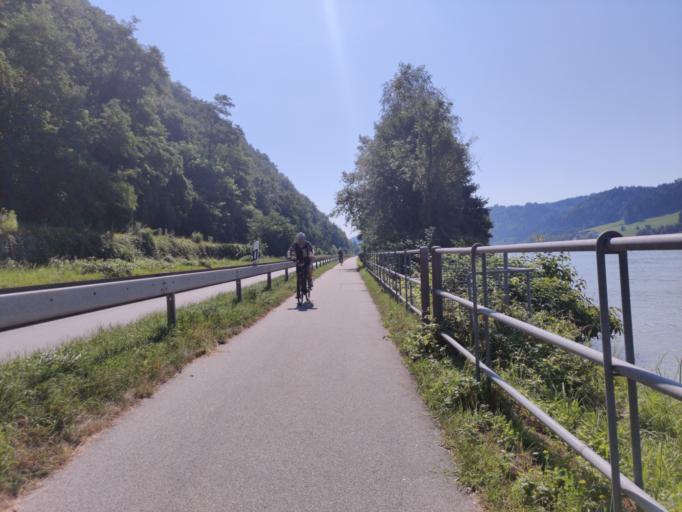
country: DE
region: Bavaria
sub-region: Lower Bavaria
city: Obernzell
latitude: 48.5659
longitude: 13.6088
